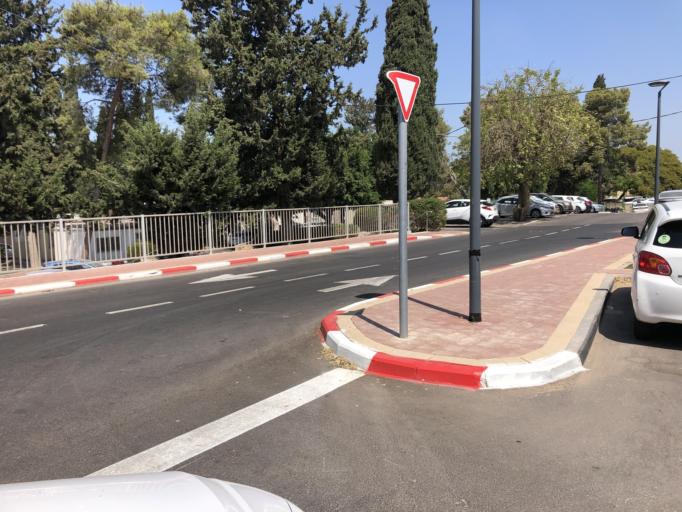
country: IL
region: Central District
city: Rosh Ha'Ayin
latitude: 32.0932
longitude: 34.9570
